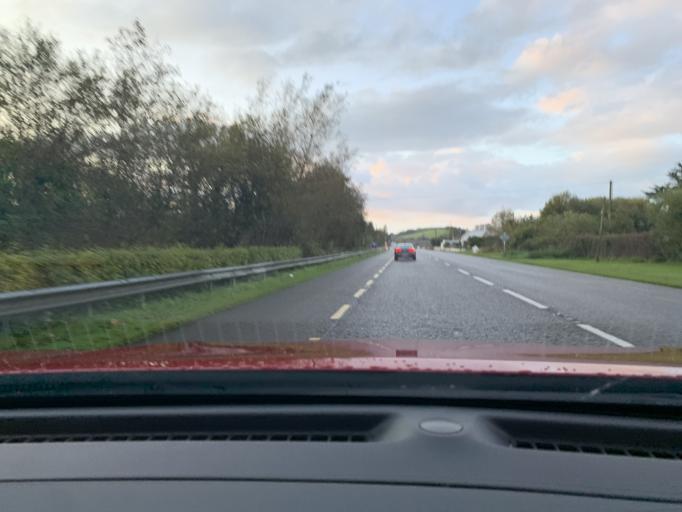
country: IE
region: Connaught
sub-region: Roscommon
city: Boyle
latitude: 54.0717
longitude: -8.3663
